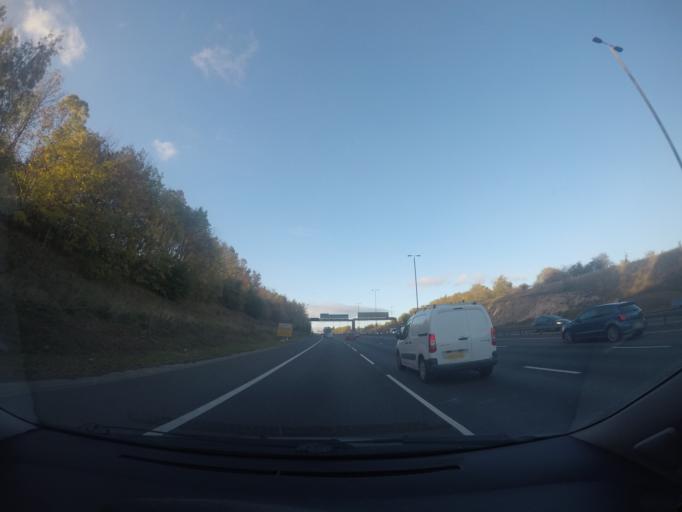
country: GB
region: England
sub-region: City and Borough of Leeds
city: Aberford
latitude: 53.8380
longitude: -1.3398
